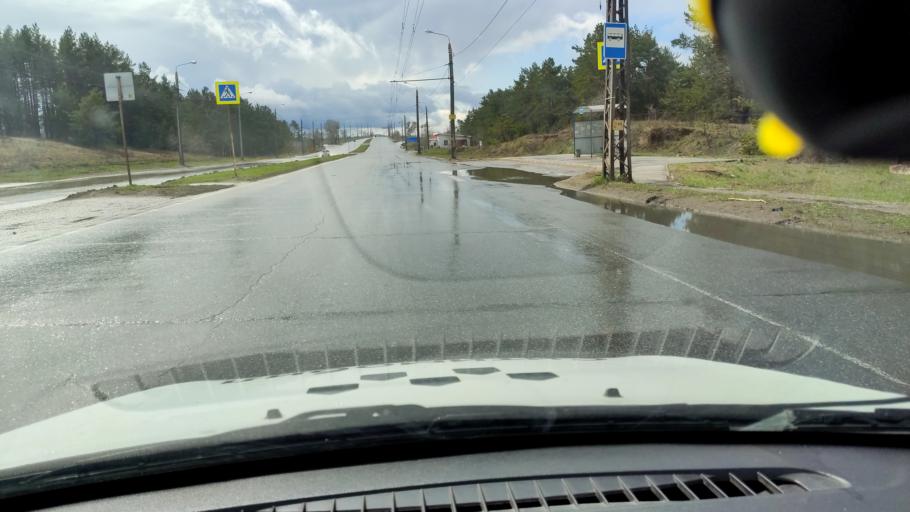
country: RU
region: Samara
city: Zhigulevsk
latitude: 53.5229
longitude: 49.5418
